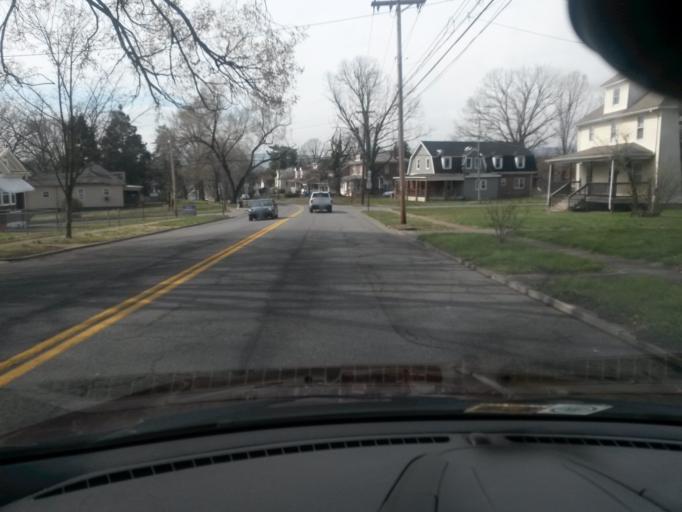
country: US
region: Virginia
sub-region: City of Roanoke
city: Roanoke
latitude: 37.2936
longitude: -79.9748
